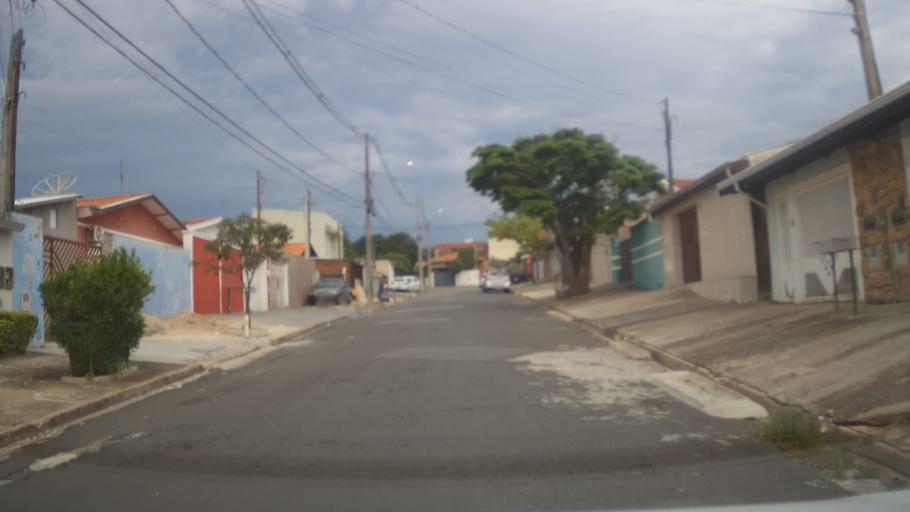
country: BR
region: Sao Paulo
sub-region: Campinas
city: Campinas
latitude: -22.9292
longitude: -47.1245
